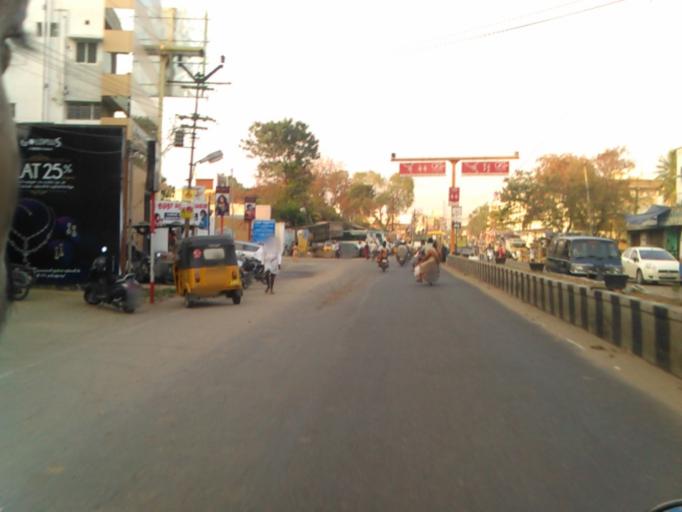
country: IN
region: Tamil Nadu
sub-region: Erode
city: Erode
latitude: 11.3463
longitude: 77.7307
